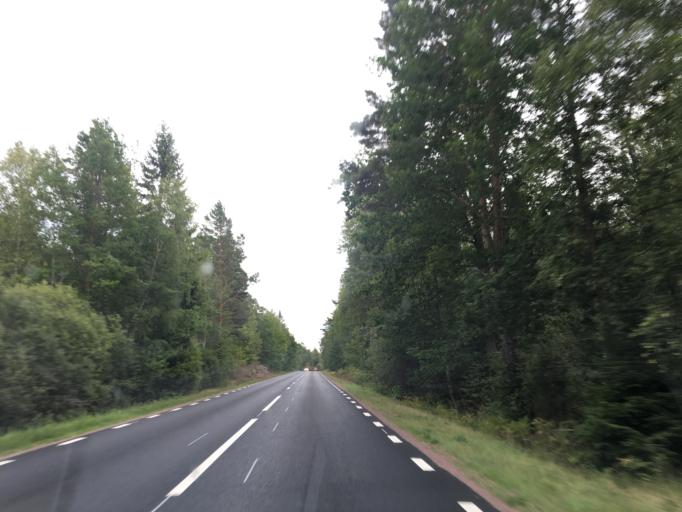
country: SE
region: Kalmar
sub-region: Nybro Kommun
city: Nybro
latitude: 56.9255
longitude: 15.9440
